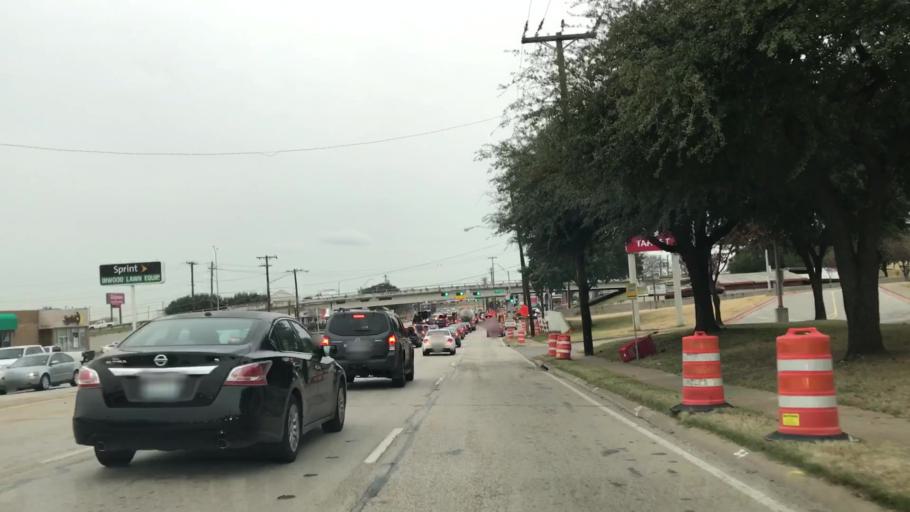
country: US
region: Texas
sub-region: Dallas County
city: University Park
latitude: 32.8617
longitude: -96.8533
